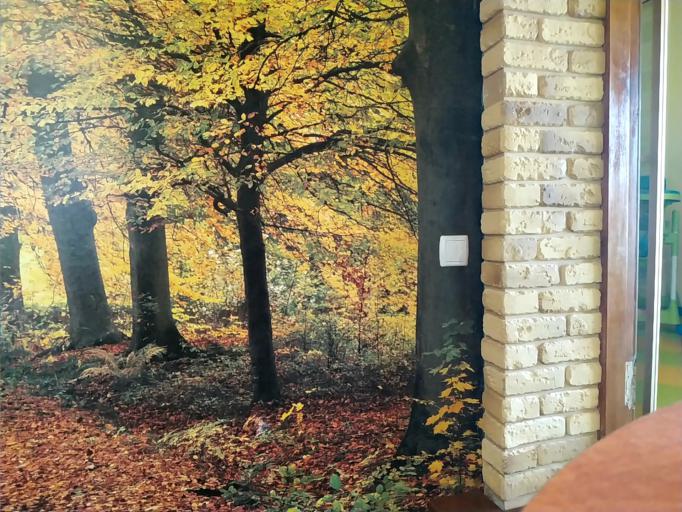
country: RU
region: Tverskaya
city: Maksatikha
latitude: 57.6124
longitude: 35.8351
